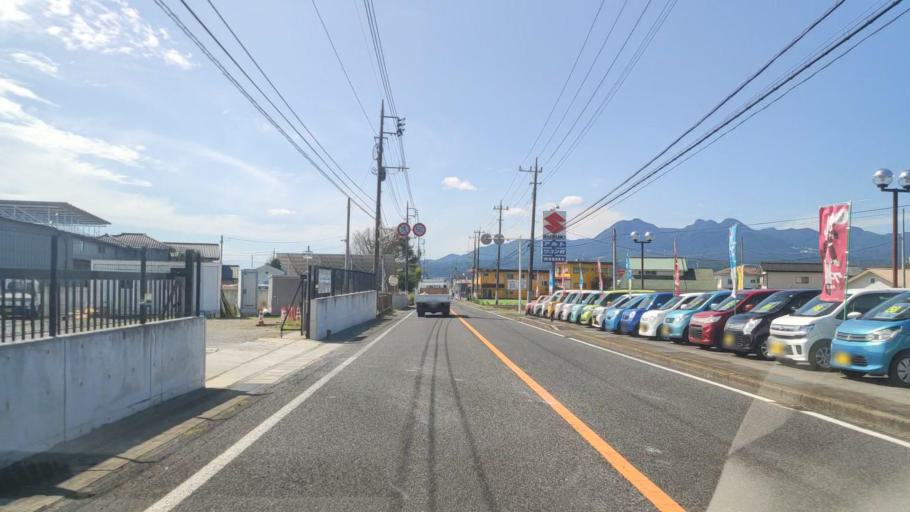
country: JP
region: Gunma
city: Shibukawa
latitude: 36.5345
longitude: 139.0195
